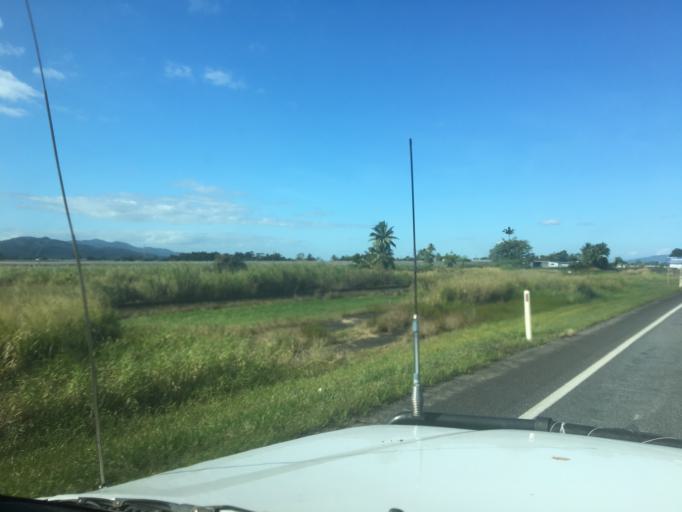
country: AU
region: Queensland
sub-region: Cassowary Coast
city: Innisfail
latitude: -17.3285
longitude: 145.9284
